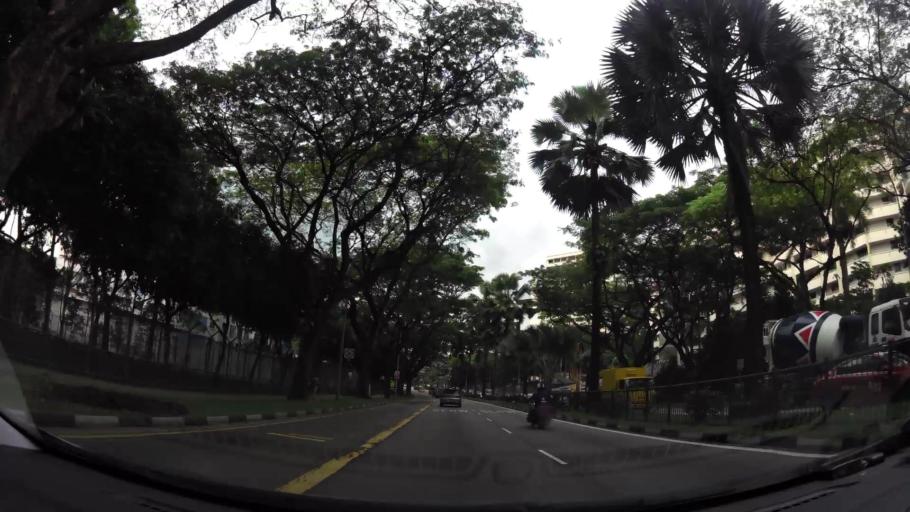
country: MY
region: Johor
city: Kampung Pasir Gudang Baru
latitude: 1.4320
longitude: 103.8266
